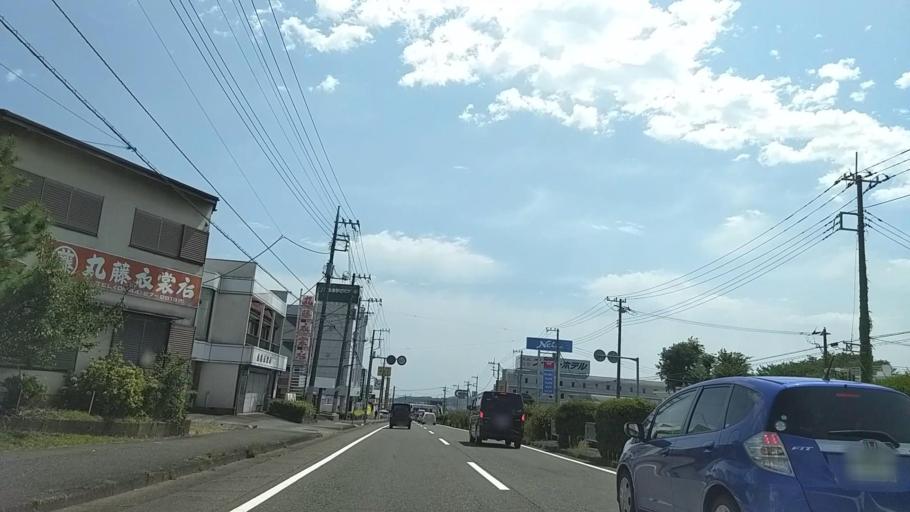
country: JP
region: Shizuoka
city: Fujinomiya
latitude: 35.2354
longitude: 138.6206
